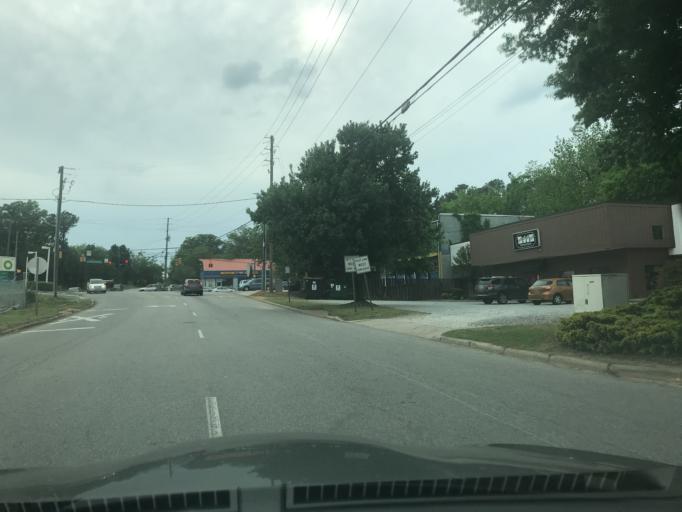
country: US
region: North Carolina
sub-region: Wake County
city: Raleigh
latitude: 35.8079
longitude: -78.6237
